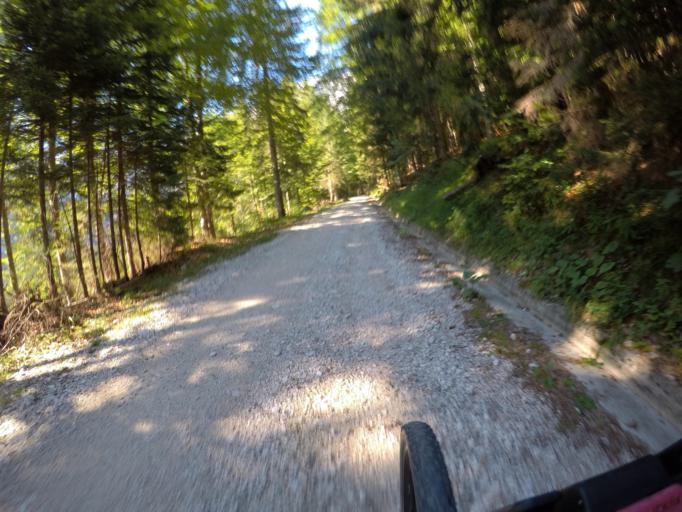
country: IT
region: Friuli Venezia Giulia
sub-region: Provincia di Udine
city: Malborghetto
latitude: 46.4559
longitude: 13.4659
